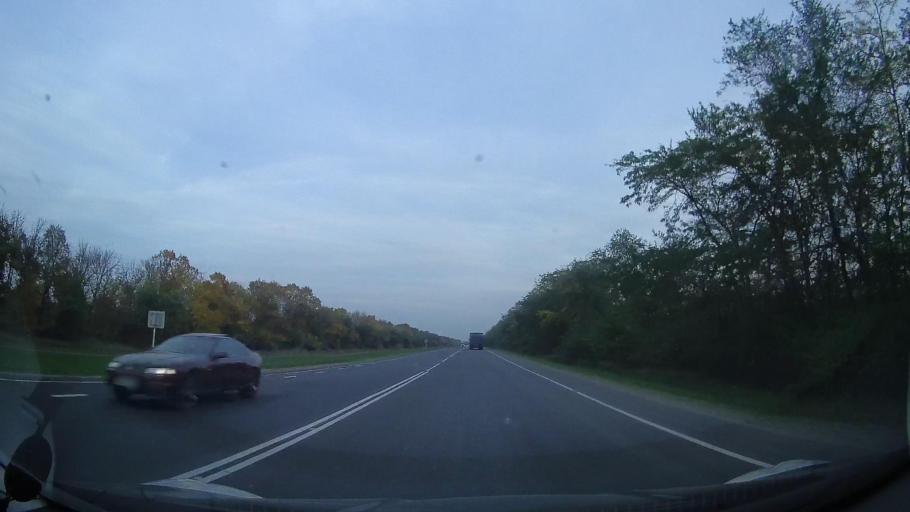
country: RU
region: Rostov
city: Kirovskaya
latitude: 47.0009
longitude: 39.9809
